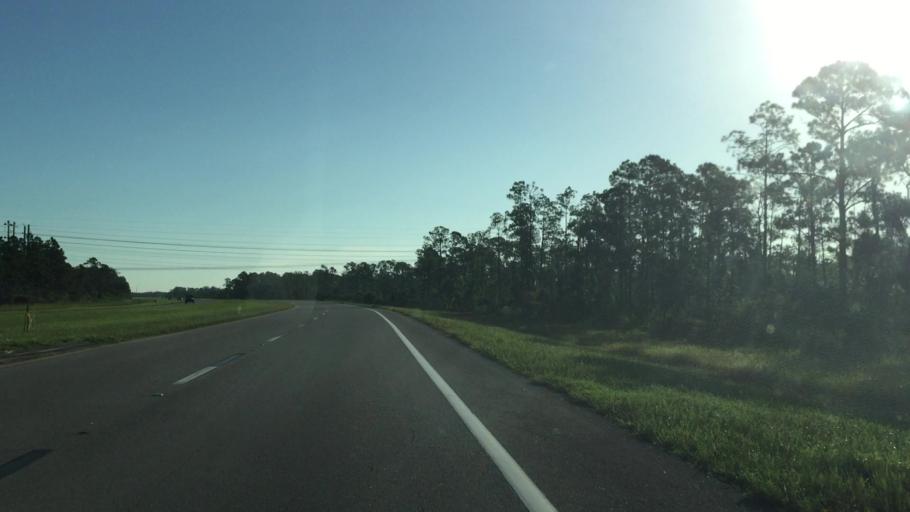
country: US
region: Florida
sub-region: Lee County
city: Gateway
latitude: 26.5662
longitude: -81.7395
